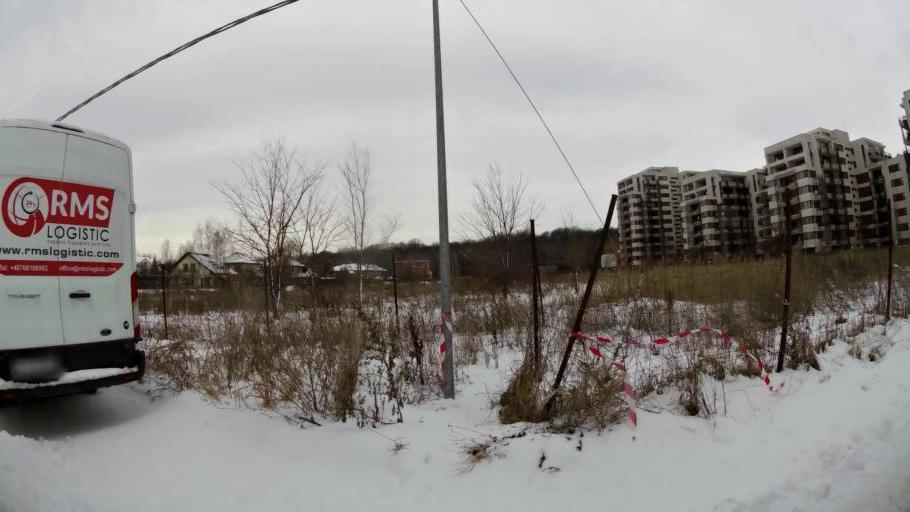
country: RO
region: Ilfov
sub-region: Comuna Tunari
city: Tunari
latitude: 44.5213
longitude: 26.1459
